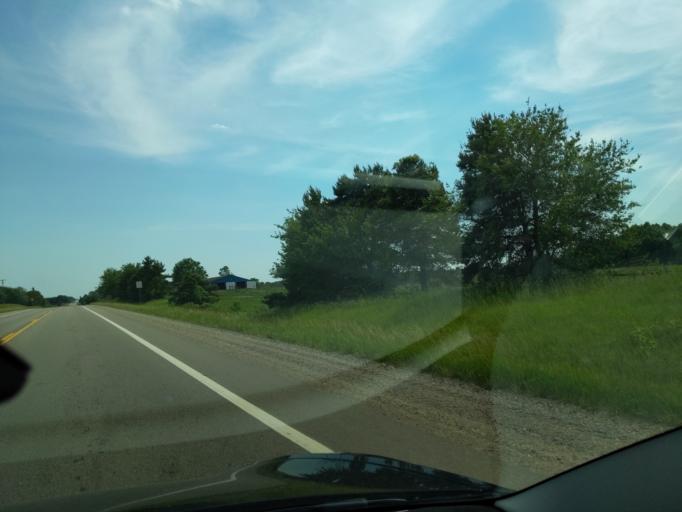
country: US
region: Michigan
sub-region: Barry County
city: Nashville
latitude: 42.6624
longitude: -85.0952
